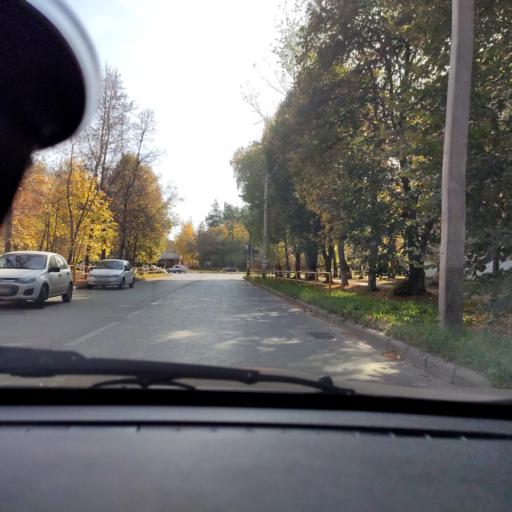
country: RU
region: Samara
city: Tol'yatti
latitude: 53.5005
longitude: 49.4094
